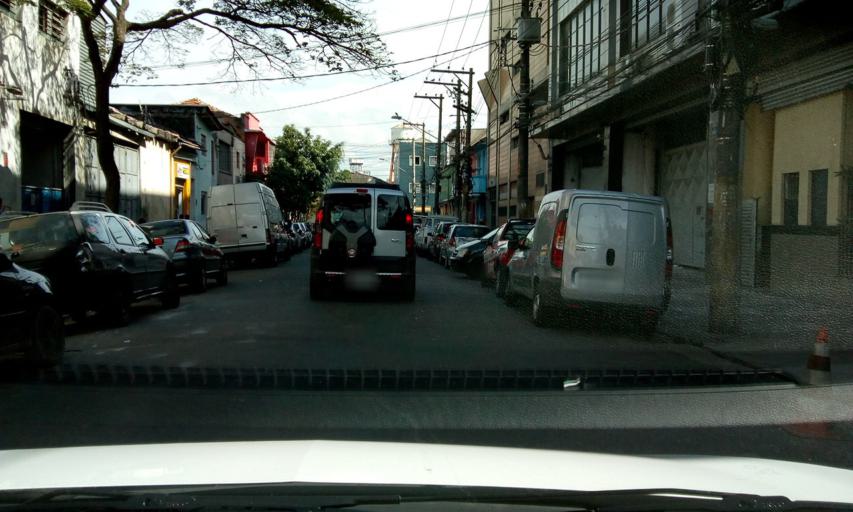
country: BR
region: Sao Paulo
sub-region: Sao Paulo
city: Sao Paulo
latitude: -23.5411
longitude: -46.6090
